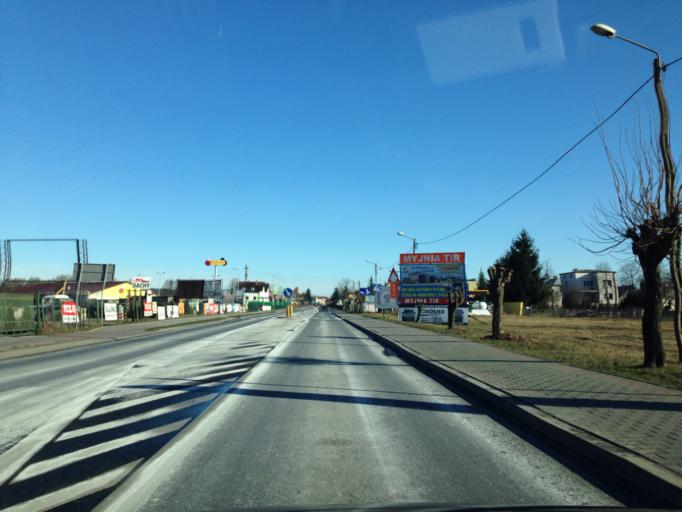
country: PL
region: Warmian-Masurian Voivodeship
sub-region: Powiat nowomiejski
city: Nowe Miasto Lubawskie
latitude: 53.4115
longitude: 19.5936
